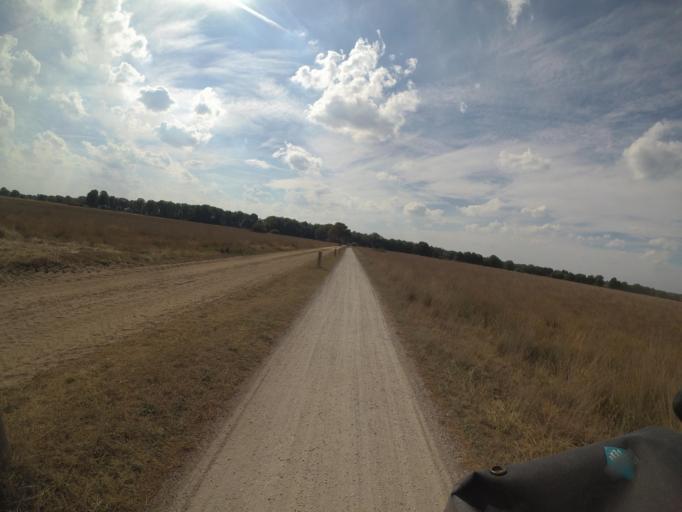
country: NL
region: Drenthe
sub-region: Gemeente De Wolden
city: Ruinen
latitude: 52.7875
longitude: 6.3818
